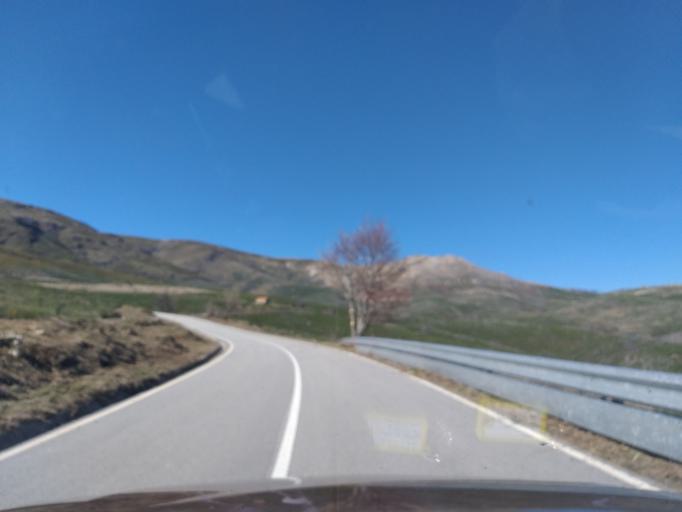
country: PT
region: Guarda
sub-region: Manteigas
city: Manteigas
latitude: 40.4599
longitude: -7.5105
